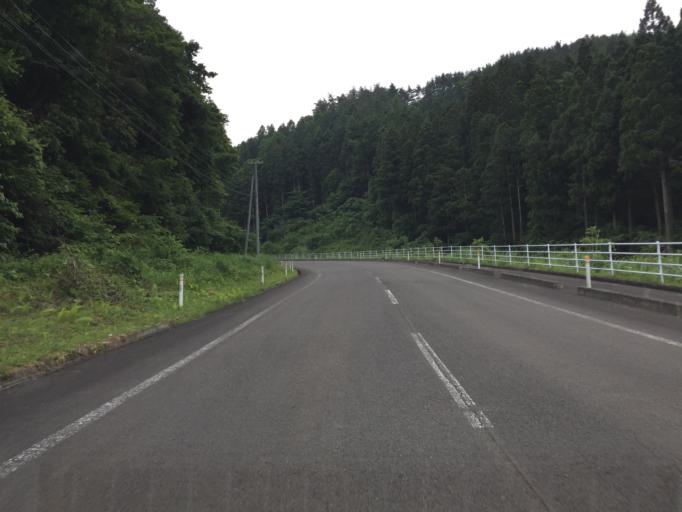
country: JP
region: Miyagi
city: Marumori
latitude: 37.8154
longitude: 140.7338
